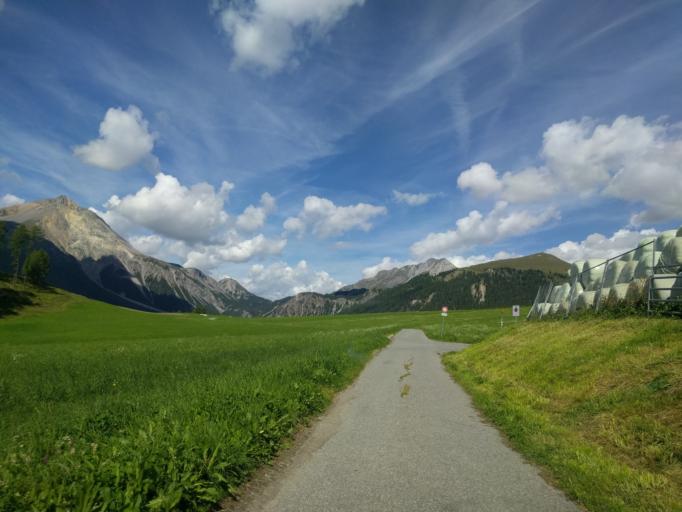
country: IT
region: Trentino-Alto Adige
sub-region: Bolzano
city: Tubre
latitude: 46.6224
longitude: 10.3687
